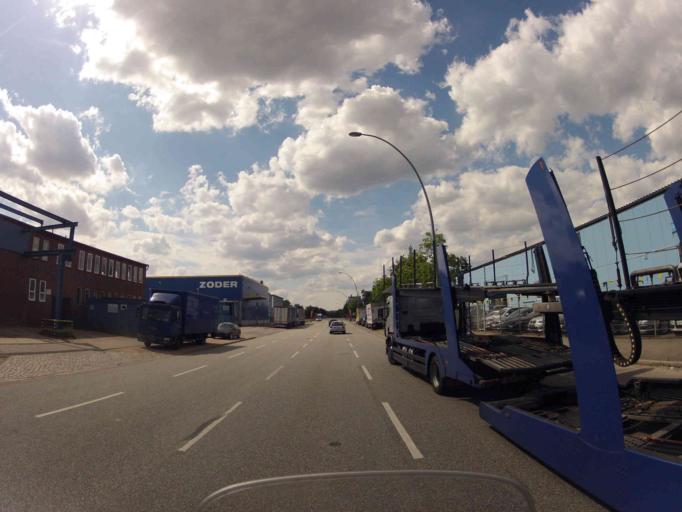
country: DE
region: Hamburg
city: Rothenburgsort
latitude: 53.5383
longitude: 10.0571
